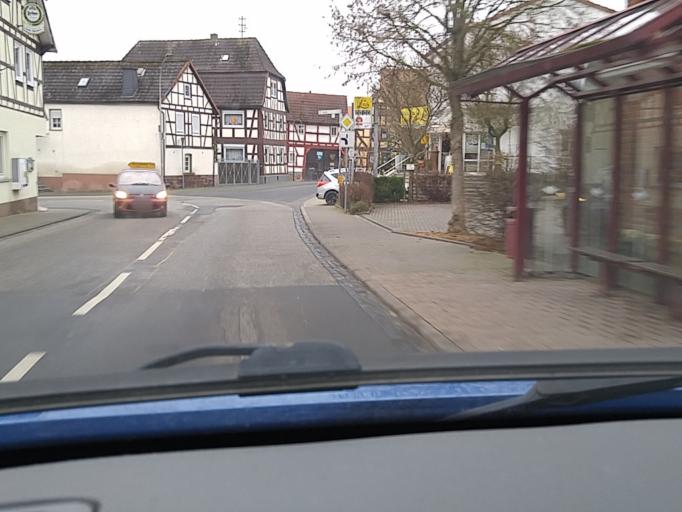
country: DE
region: Hesse
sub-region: Regierungsbezirk Darmstadt
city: Ranstadt
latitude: 50.3639
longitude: 8.9586
